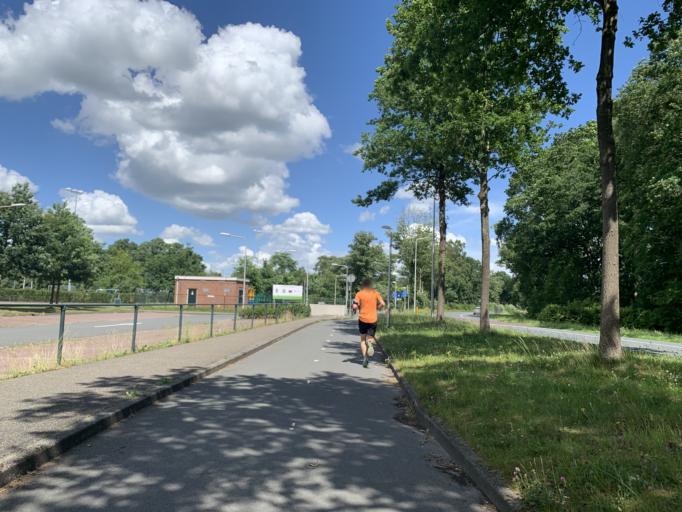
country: NL
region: Groningen
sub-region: Gemeente Haren
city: Haren
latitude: 53.1631
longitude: 6.6194
